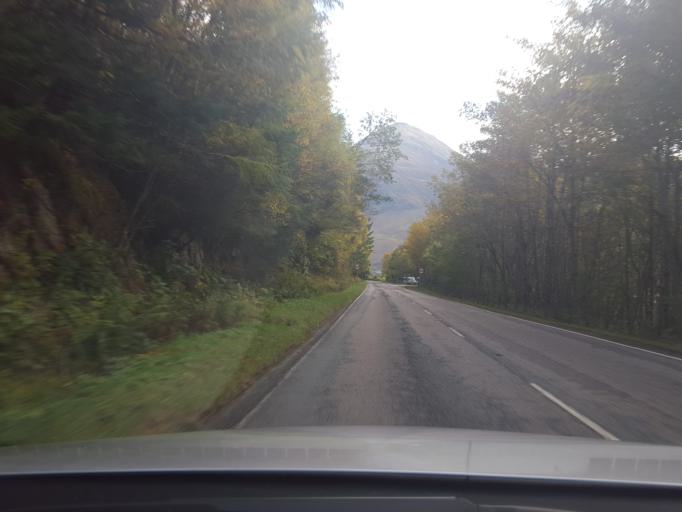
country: GB
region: Scotland
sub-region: Highland
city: Fort William
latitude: 57.2353
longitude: -5.4309
